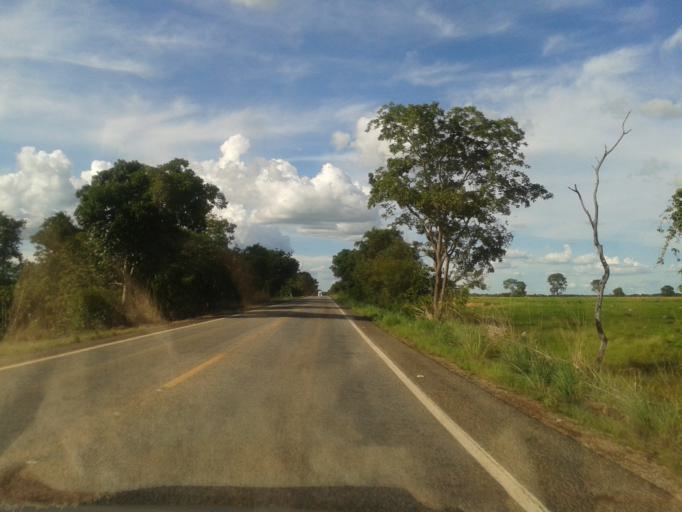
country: BR
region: Goias
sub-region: Mozarlandia
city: Mozarlandia
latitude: -14.5077
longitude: -50.4850
